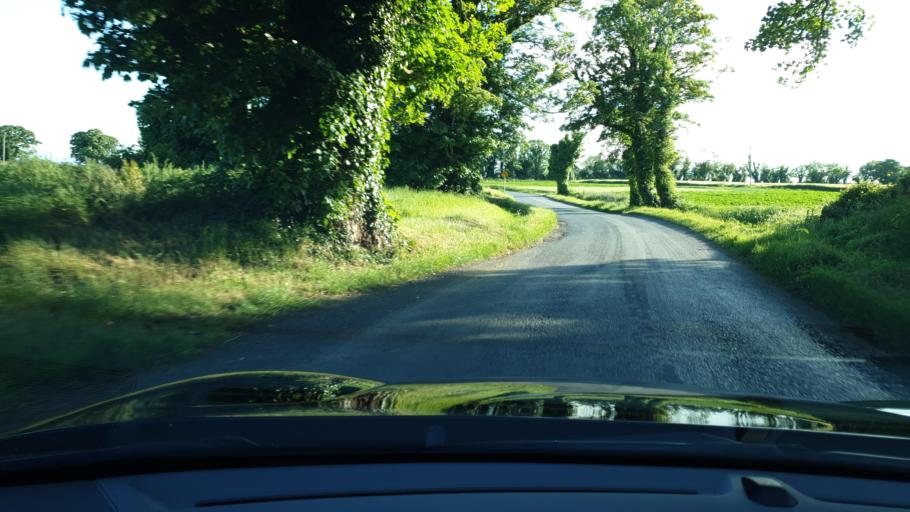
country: IE
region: Leinster
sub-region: Fingal County
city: Swords
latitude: 53.5051
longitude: -6.2390
